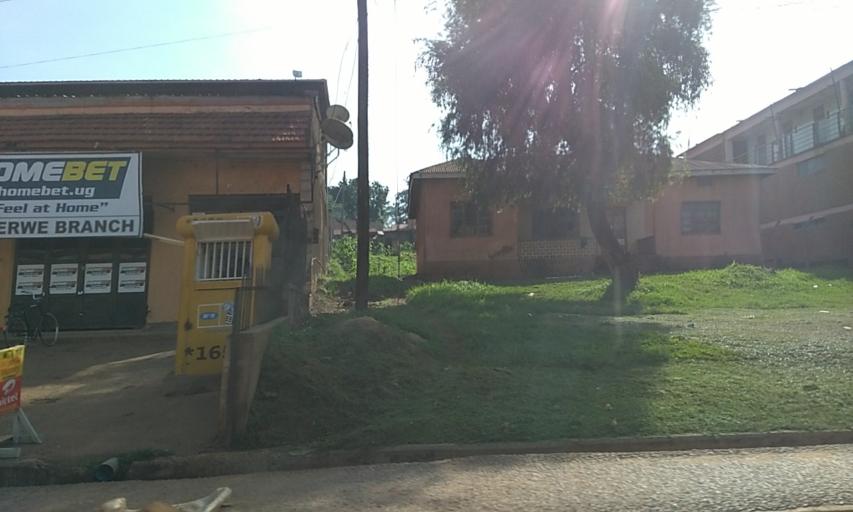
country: UG
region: Central Region
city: Kampala Central Division
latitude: 0.3451
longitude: 32.5713
